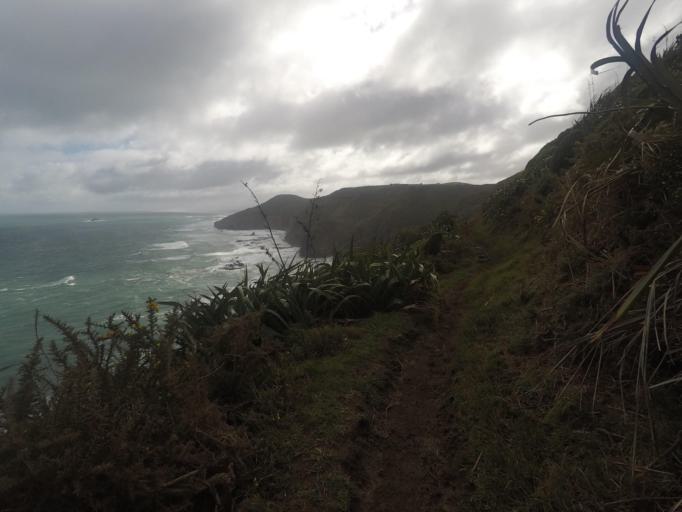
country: NZ
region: Auckland
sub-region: Auckland
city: Muriwai Beach
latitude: -36.8716
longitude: 174.4335
